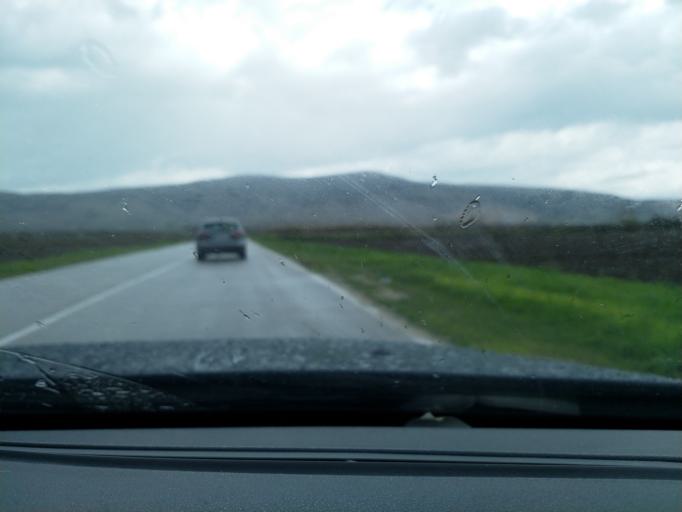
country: GR
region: Thessaly
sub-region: Trikala
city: Taxiarches
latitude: 39.5525
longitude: 21.8895
